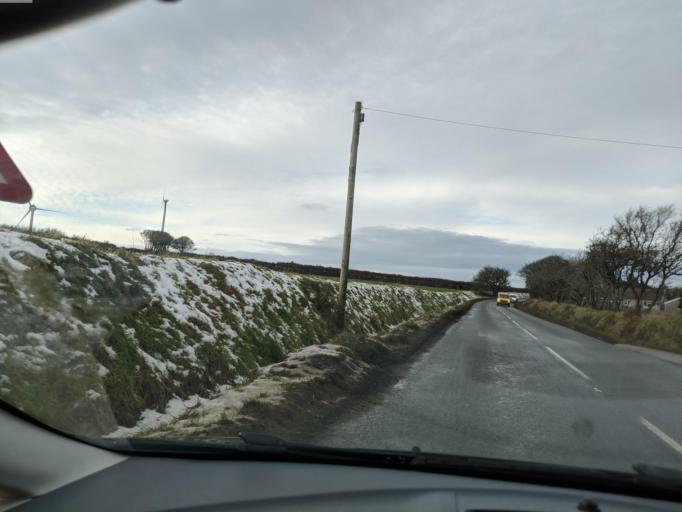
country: GB
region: England
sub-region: Cornwall
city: Jacobstow
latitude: 50.6647
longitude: -4.5914
